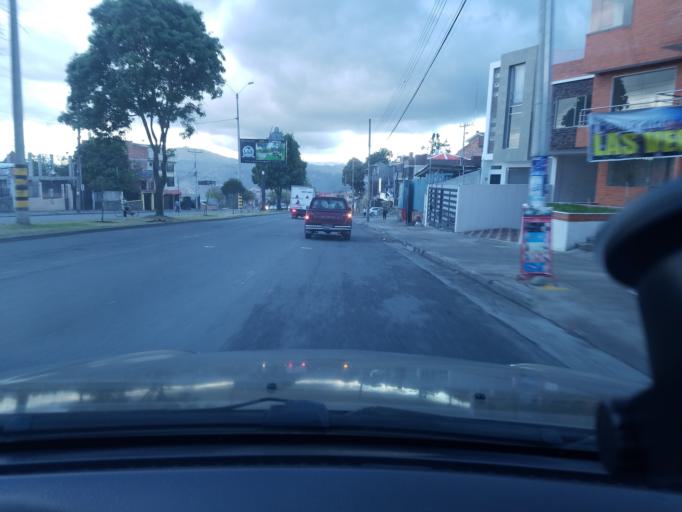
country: EC
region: Azuay
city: Cuenca
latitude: -2.8848
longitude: -79.0014
